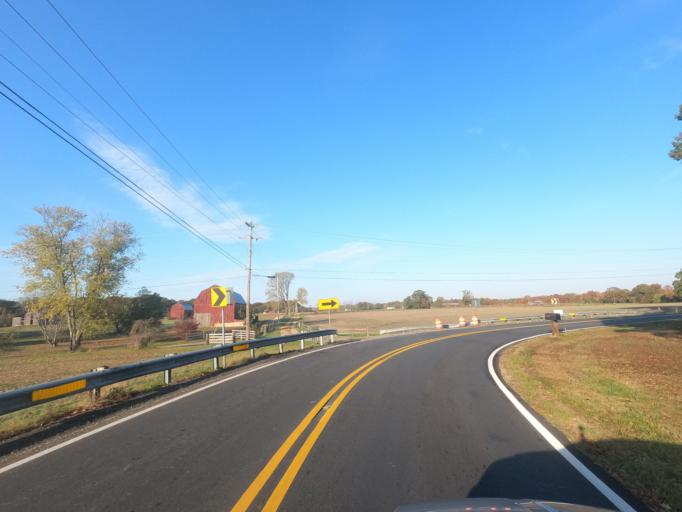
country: US
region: Maryland
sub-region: Saint Mary's County
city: Golden Beach
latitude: 38.4994
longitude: -76.6412
